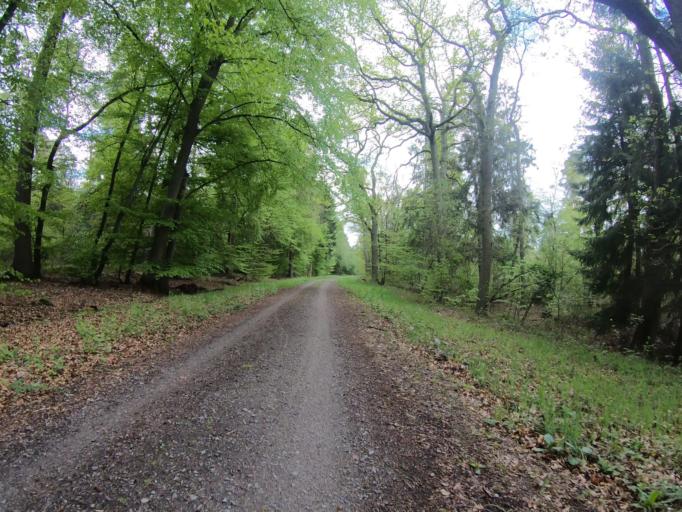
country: DE
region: Lower Saxony
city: Gifhorn
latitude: 52.5010
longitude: 10.5663
